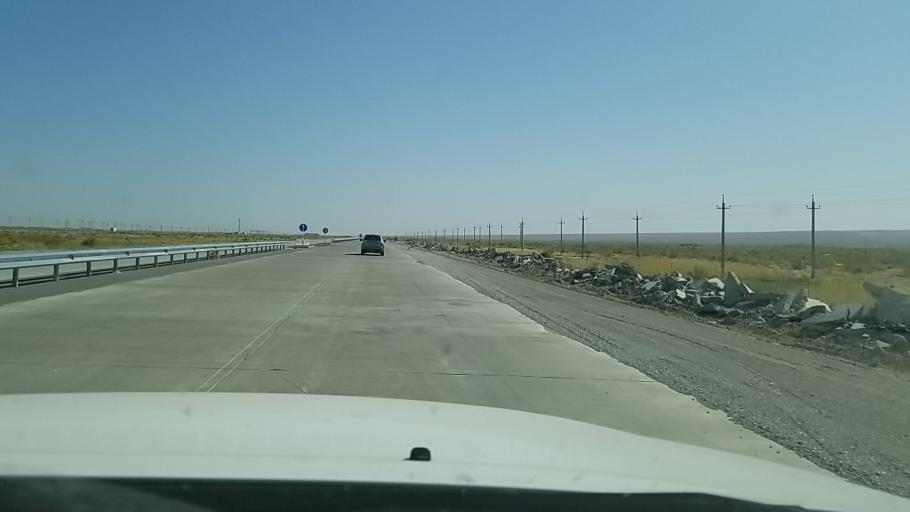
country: KZ
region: Almaty Oblysy
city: Kegen
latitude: 43.7463
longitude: 78.8620
